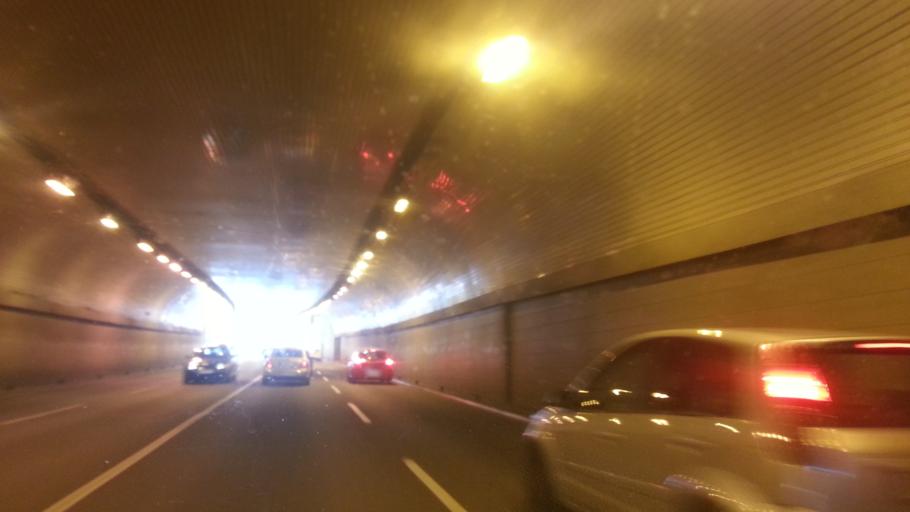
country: RS
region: Central Serbia
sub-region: Belgrade
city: Stari Grad
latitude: 44.8142
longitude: 20.4597
